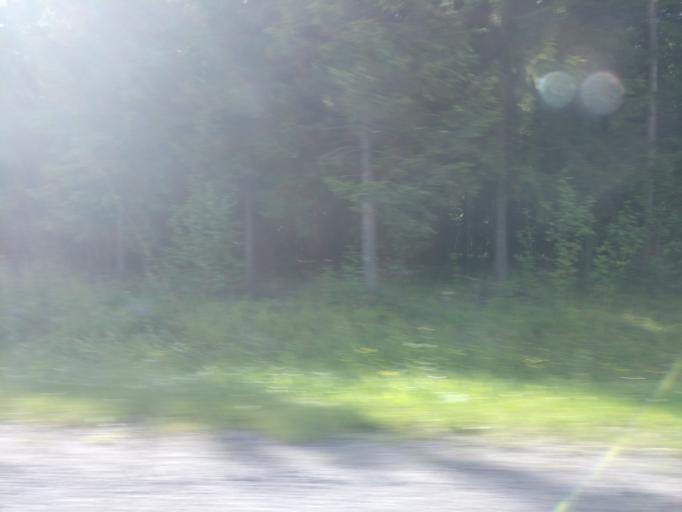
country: FI
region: Uusimaa
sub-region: Helsinki
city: Hyvinge
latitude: 60.5948
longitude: 24.8540
